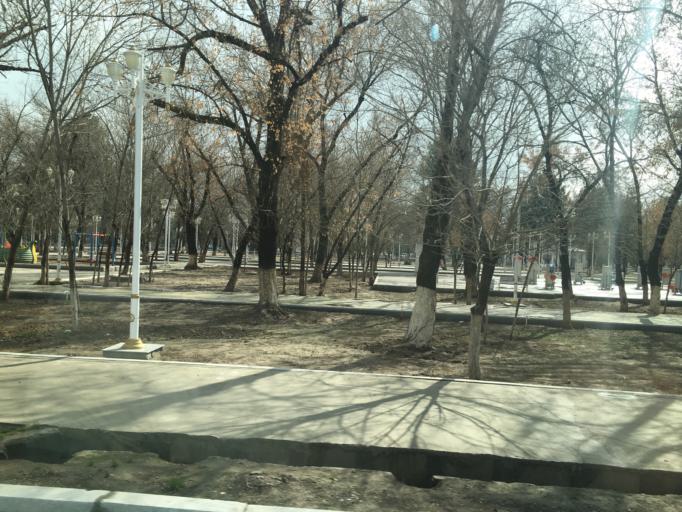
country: TM
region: Ahal
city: Ashgabat
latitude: 37.9504
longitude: 58.3622
